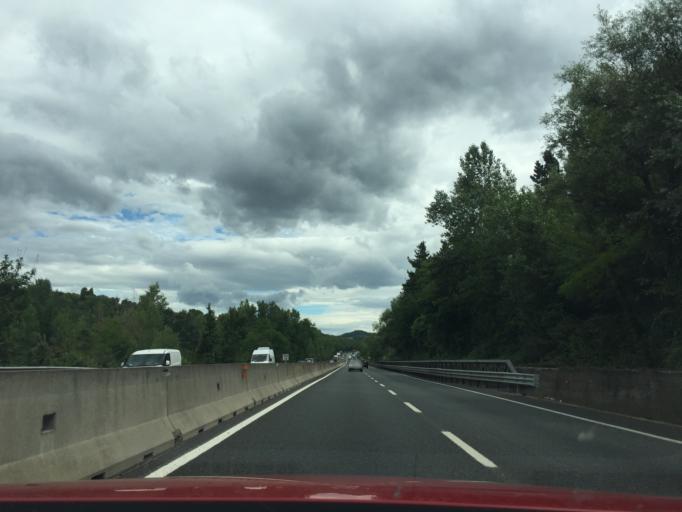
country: IT
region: Tuscany
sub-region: Province of Florence
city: Ginestra Fiorentina
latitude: 43.7149
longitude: 11.0723
